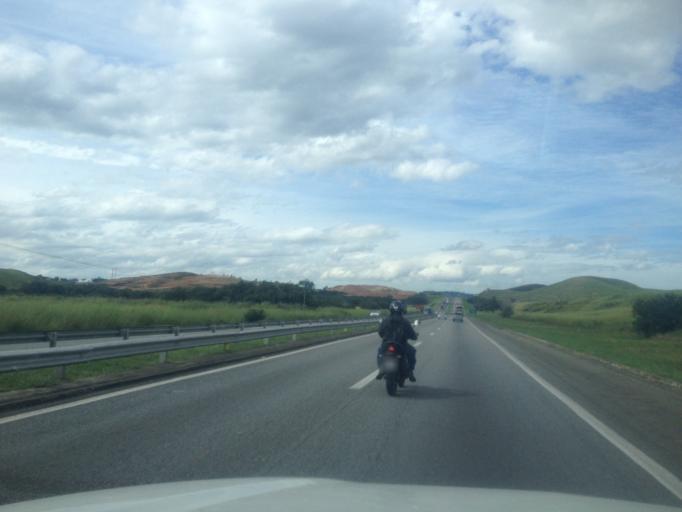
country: BR
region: Rio de Janeiro
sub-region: Porto Real
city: Porto Real
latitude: -22.4510
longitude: -44.3395
